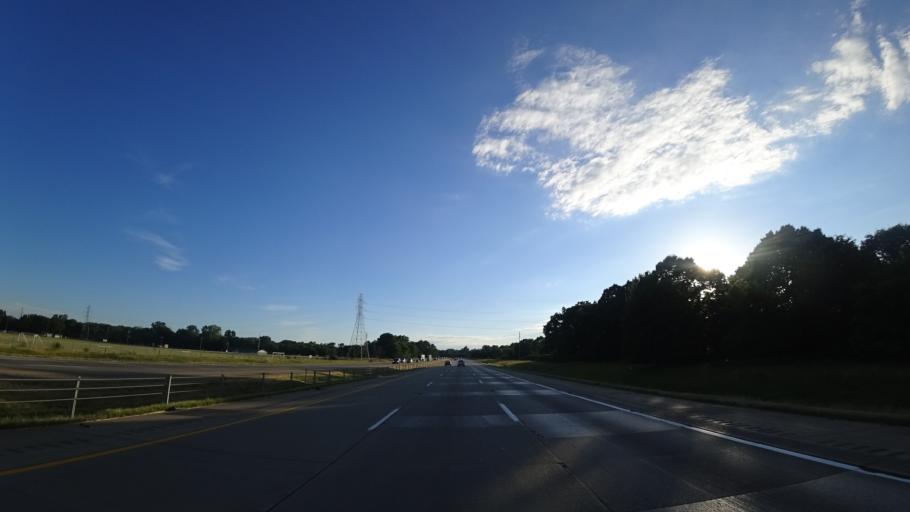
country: US
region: Michigan
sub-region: Berrien County
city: Fair Plain
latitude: 42.0546
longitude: -86.4777
